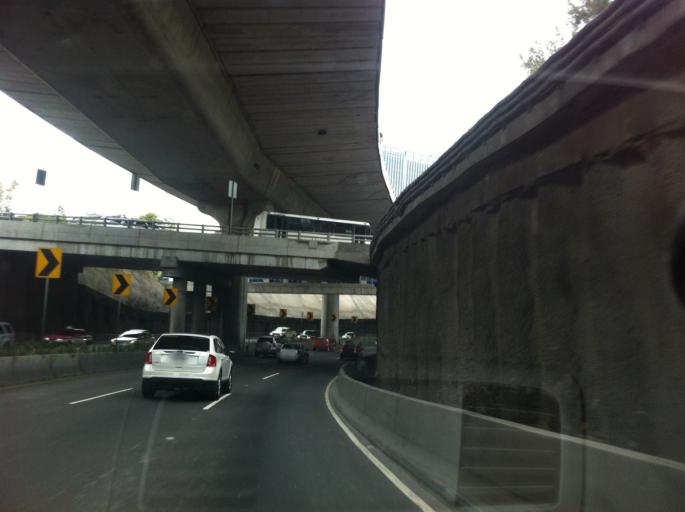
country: MX
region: Mexico City
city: Polanco
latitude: 19.4229
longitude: -99.1982
